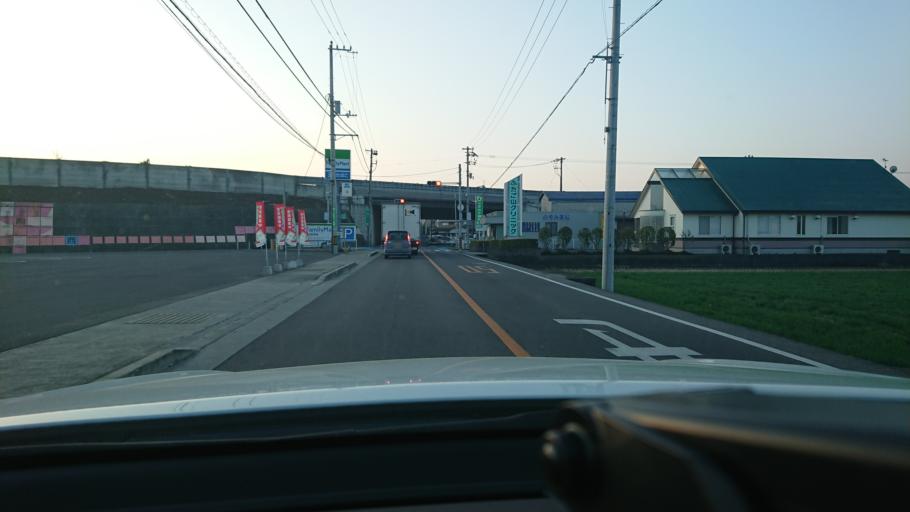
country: JP
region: Kagawa
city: Marugame
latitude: 34.2682
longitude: 133.8212
